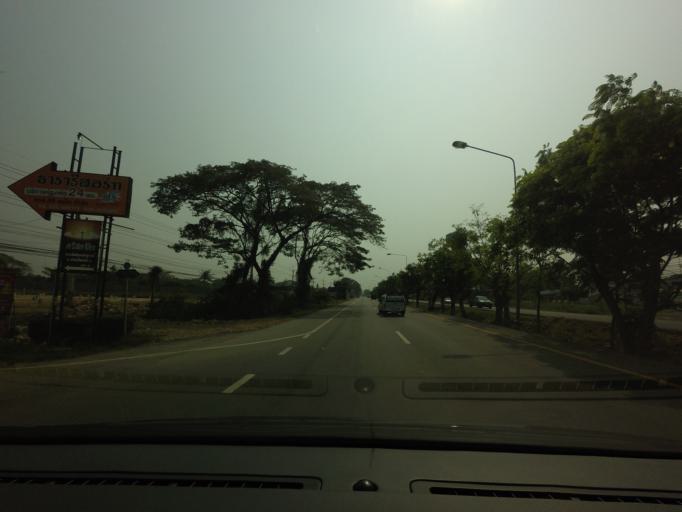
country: TH
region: Prachuap Khiri Khan
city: Sam Roi Yot
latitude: 12.2023
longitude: 99.8571
